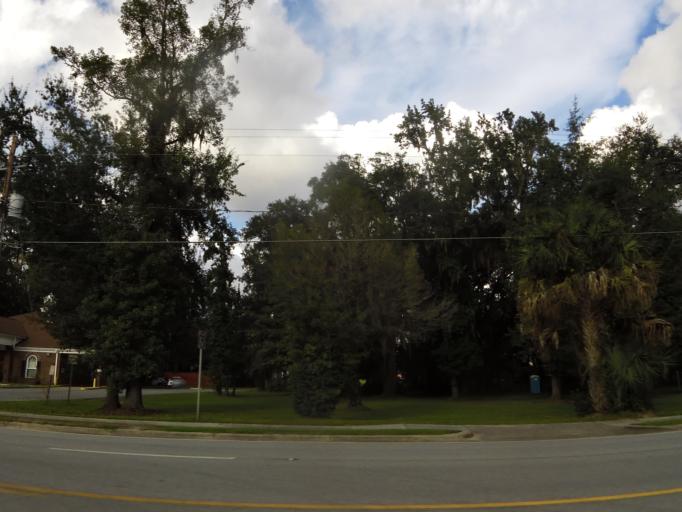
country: US
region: Georgia
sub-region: Liberty County
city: Midway
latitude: 31.7393
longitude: -81.4371
